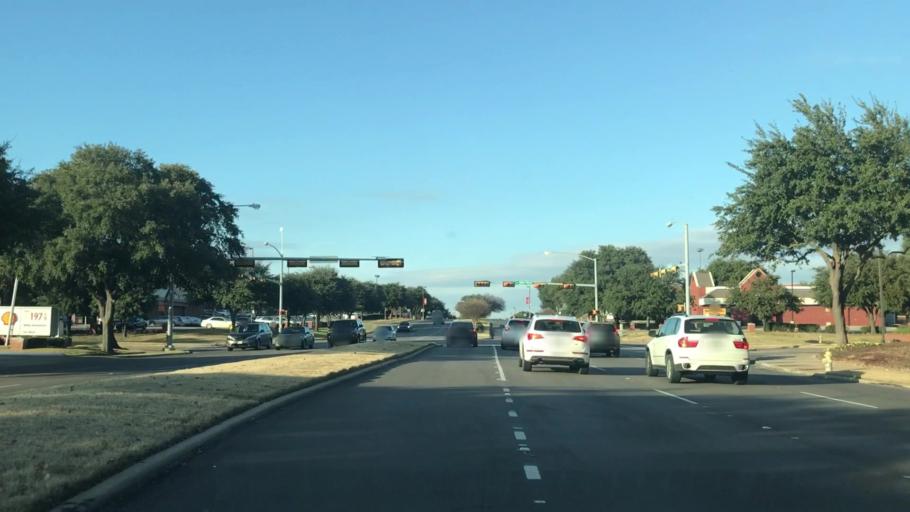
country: US
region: Texas
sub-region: Dallas County
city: Farmers Branch
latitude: 32.9399
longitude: -96.9521
